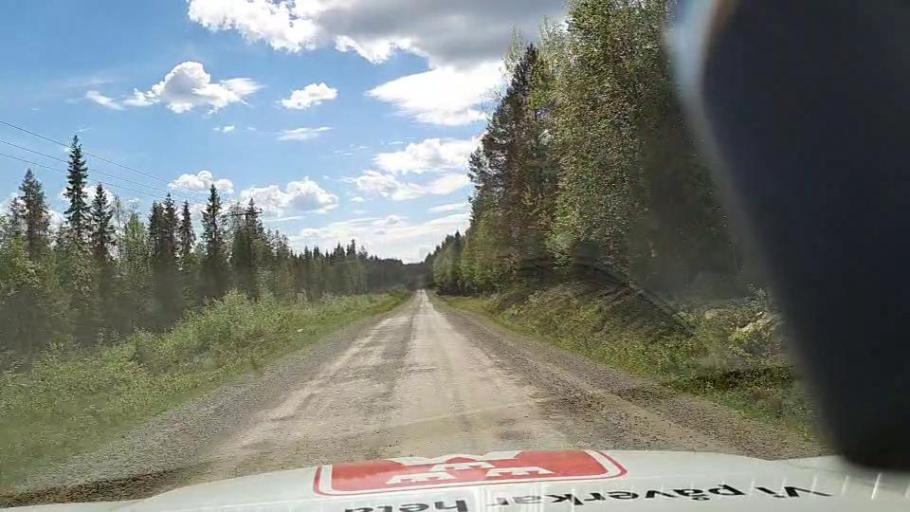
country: SE
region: Jaemtland
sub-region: Stroemsunds Kommun
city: Stroemsund
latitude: 64.5383
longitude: 15.6020
